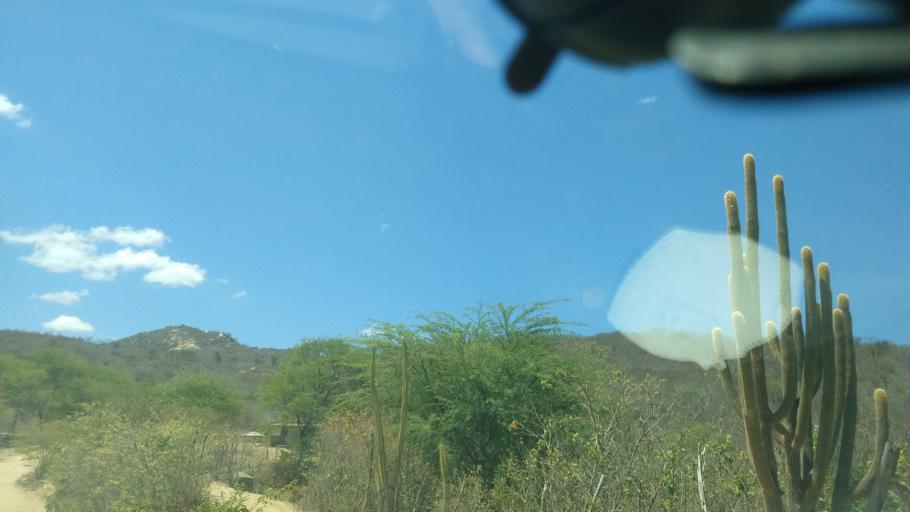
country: BR
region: Rio Grande do Norte
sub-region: Cerro Cora
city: Cerro Cora
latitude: -6.0155
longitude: -36.3114
